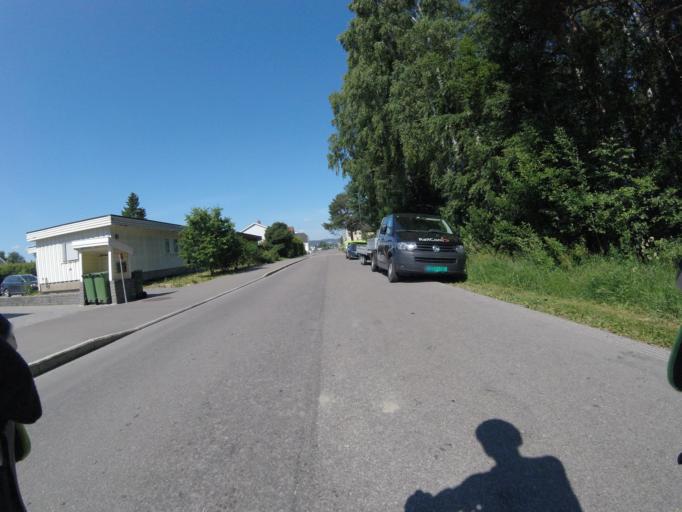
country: NO
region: Akershus
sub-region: Skedsmo
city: Lillestrom
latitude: 59.9629
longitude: 11.0531
